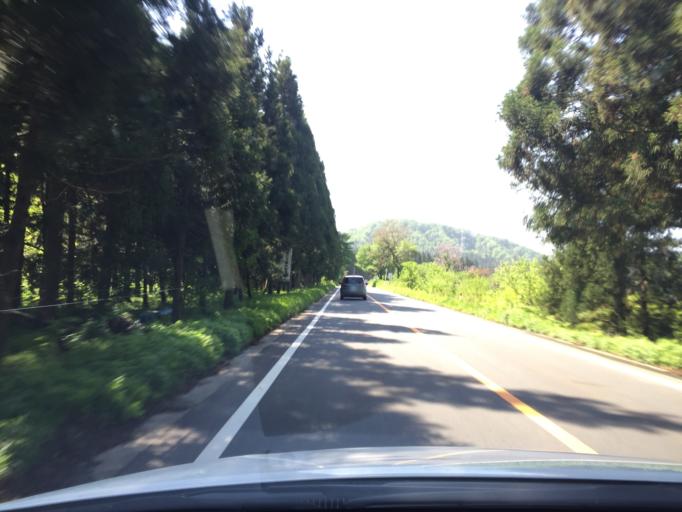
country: JP
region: Niigata
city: Muramatsu
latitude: 37.6621
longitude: 139.1380
